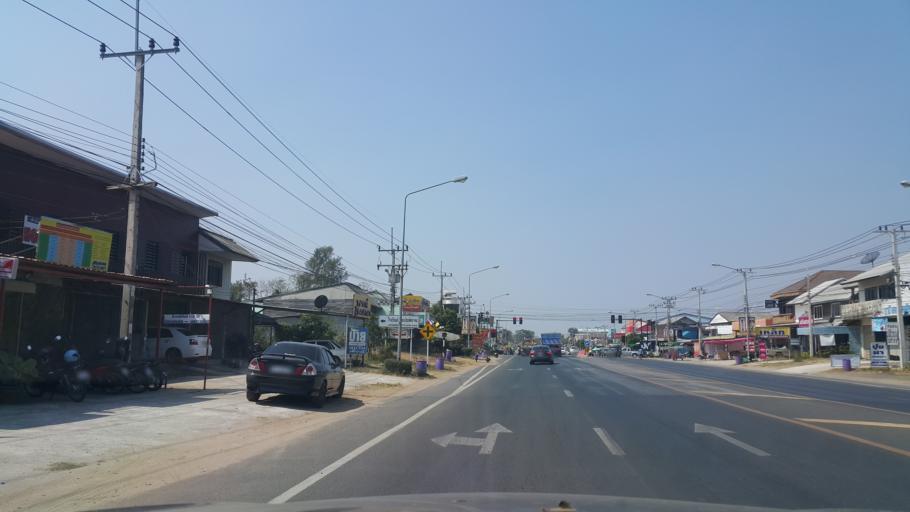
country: TH
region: Nakhon Ratchasima
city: Lam Thamen Chai
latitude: 15.3551
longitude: 102.9131
